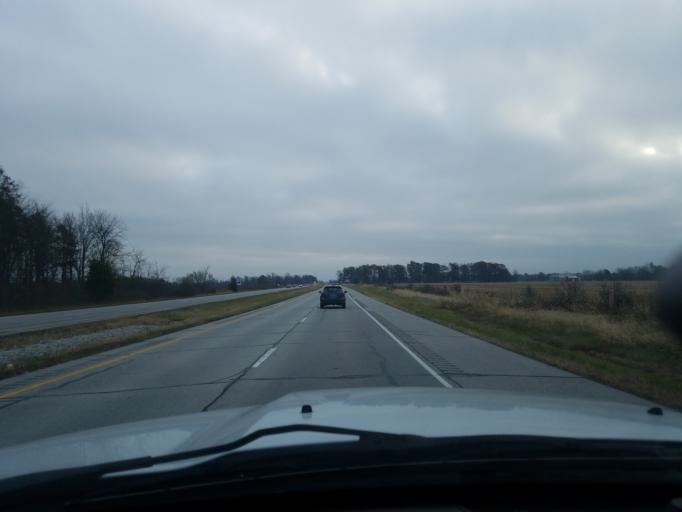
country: US
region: Indiana
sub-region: Delaware County
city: Yorktown
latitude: 40.2191
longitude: -85.5090
